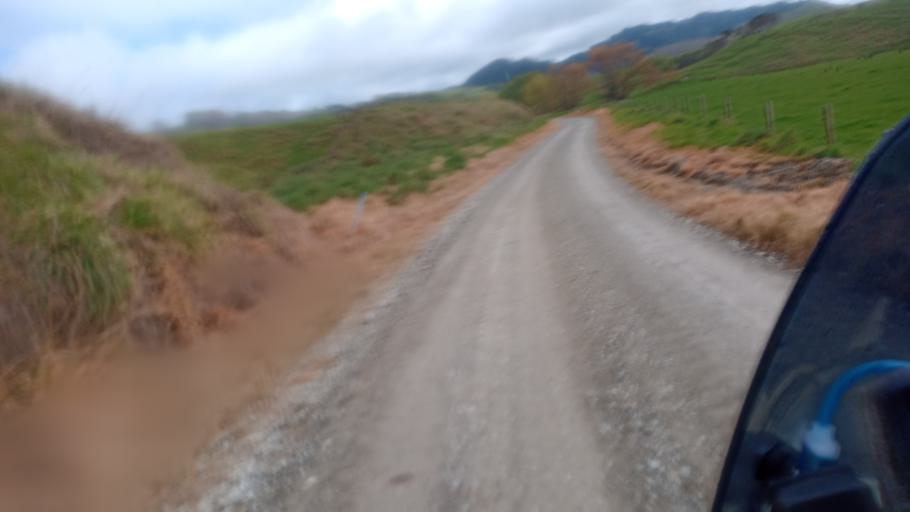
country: NZ
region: Gisborne
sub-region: Gisborne District
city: Gisborne
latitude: -38.5881
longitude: 178.1692
